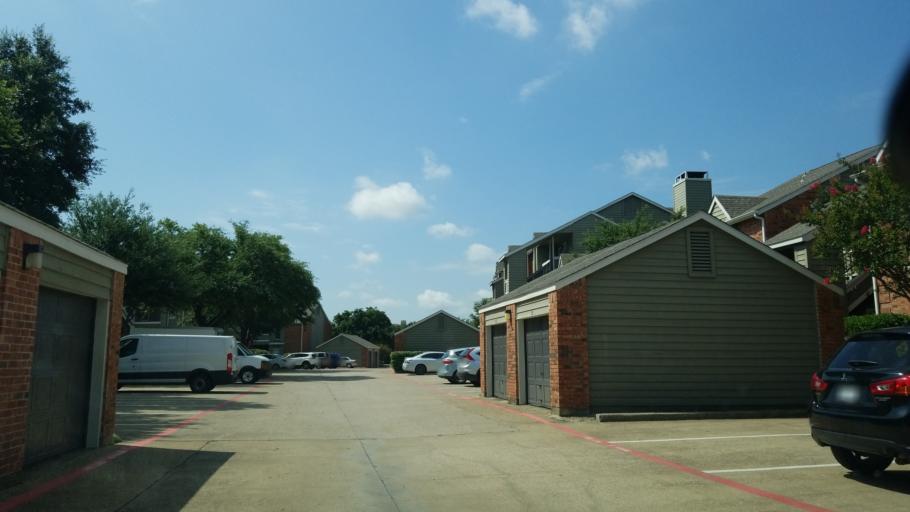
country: US
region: Texas
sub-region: Dallas County
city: Farmers Branch
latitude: 32.9288
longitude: -96.9571
